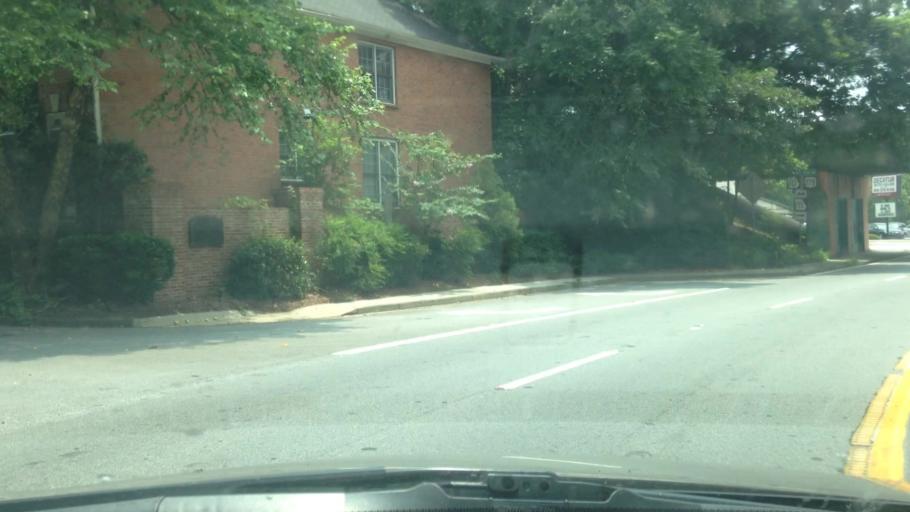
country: US
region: Georgia
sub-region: DeKalb County
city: Decatur
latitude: 33.7744
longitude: -84.2908
